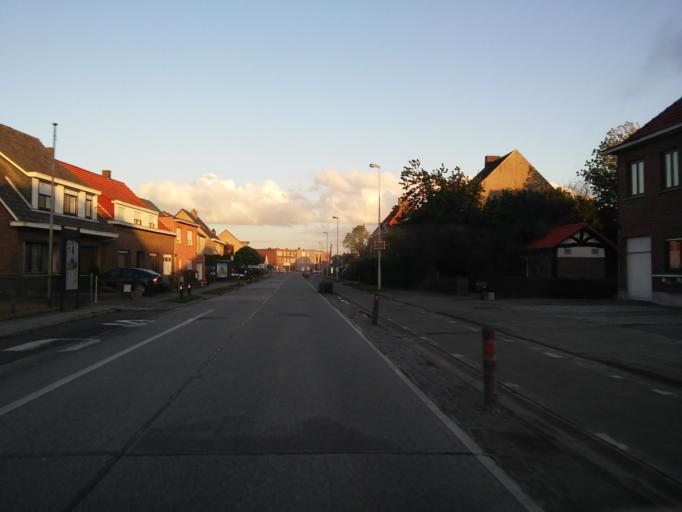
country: BE
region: Flanders
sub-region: Provincie Antwerpen
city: Aartselaar
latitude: 51.1236
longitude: 4.3915
